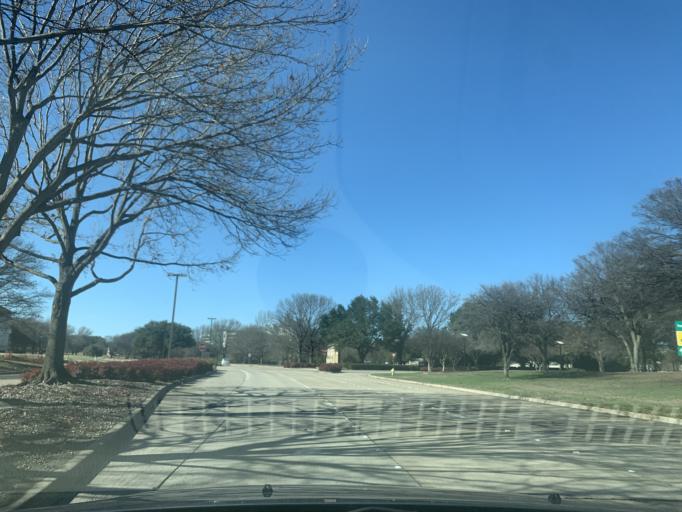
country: US
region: Texas
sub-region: Denton County
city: The Colony
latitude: 33.0696
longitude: -96.8094
